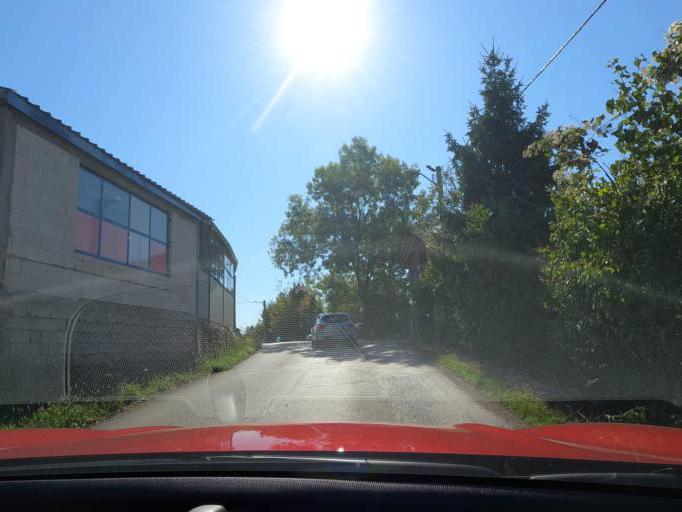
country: RS
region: Central Serbia
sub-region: Raski Okrug
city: Kraljevo
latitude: 43.7634
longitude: 20.6746
